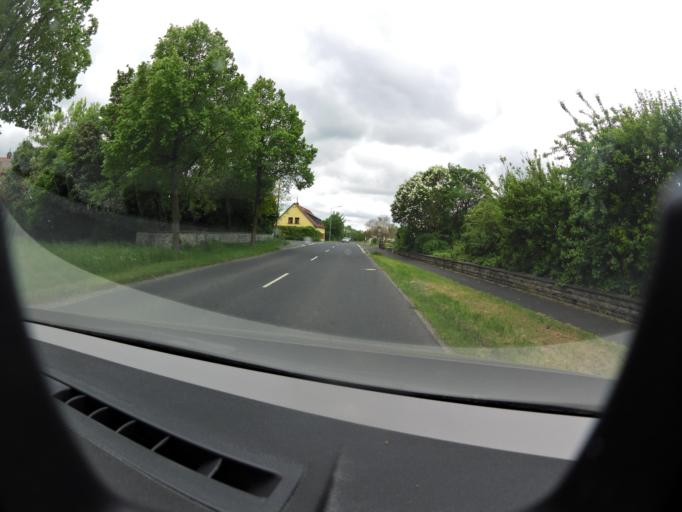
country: DE
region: Bavaria
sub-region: Regierungsbezirk Unterfranken
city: Iphofen
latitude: 49.7039
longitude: 10.2675
